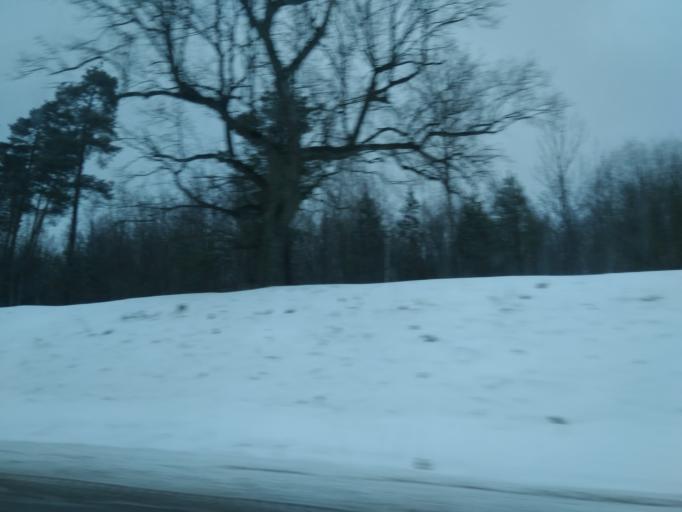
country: BY
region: Minsk
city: Nyasvizh
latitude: 53.2597
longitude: 26.6116
